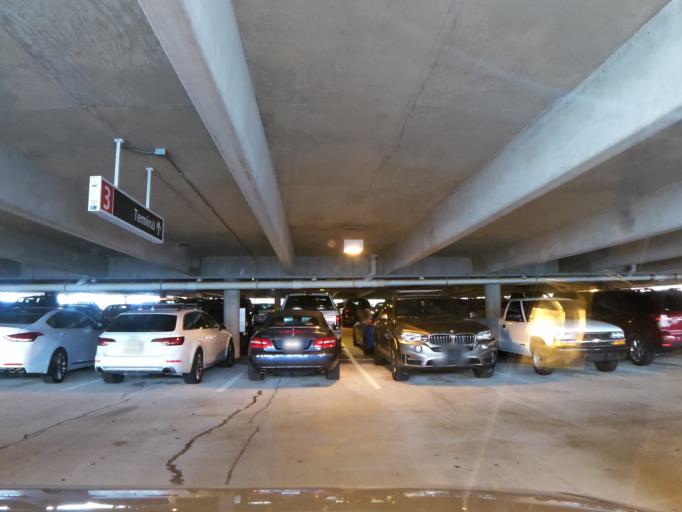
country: US
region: Florida
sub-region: Nassau County
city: Nassau Village-Ratliff
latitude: 30.4914
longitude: -81.6822
